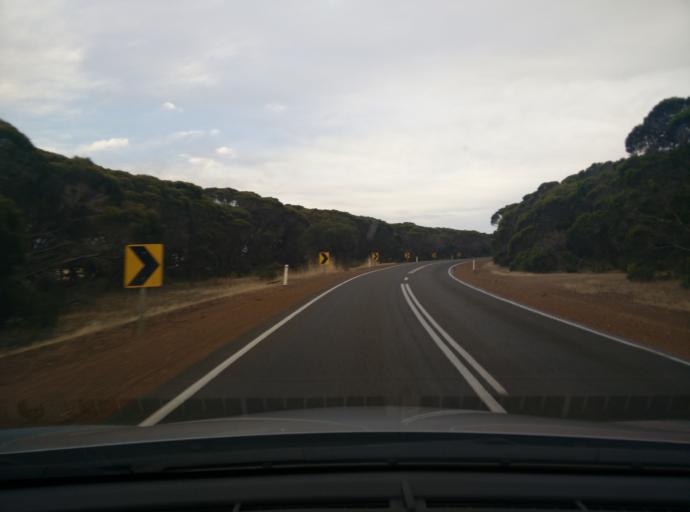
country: AU
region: South Australia
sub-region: Kangaroo Island
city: Kingscote
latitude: -35.7182
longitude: 137.5597
